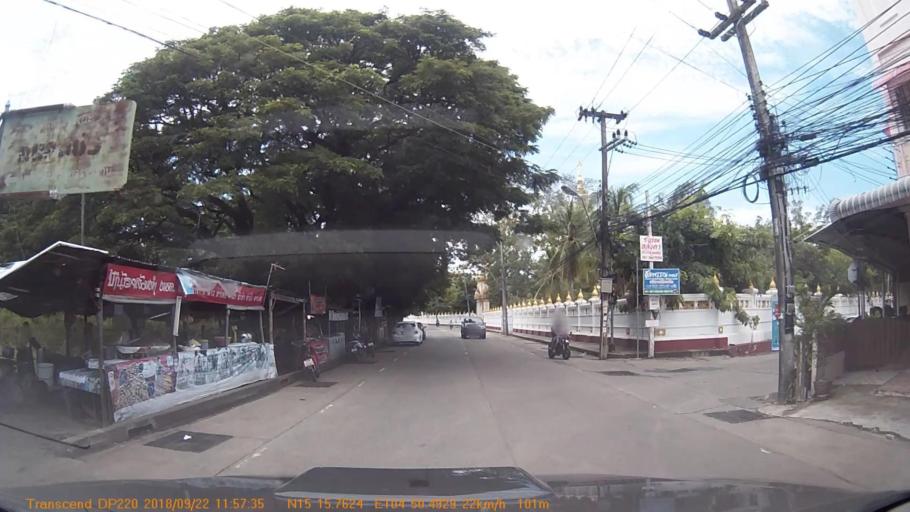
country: TH
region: Changwat Ubon Ratchathani
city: Ubon Ratchathani
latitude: 15.2627
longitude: 104.8415
